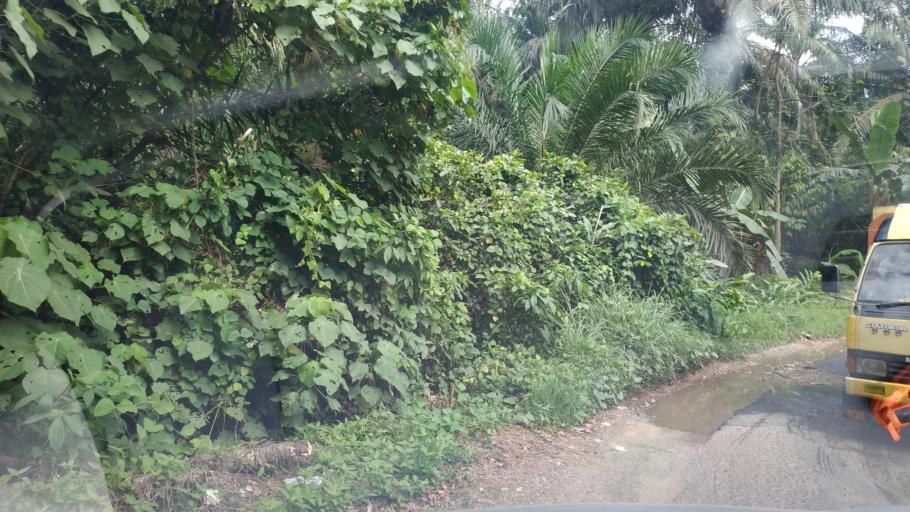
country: ID
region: North Sumatra
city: Binanga
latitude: 1.2394
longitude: 99.7507
